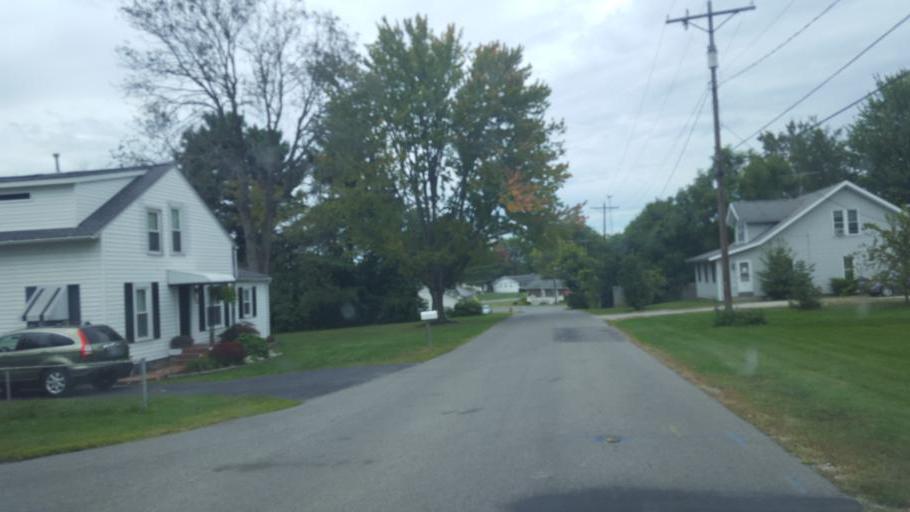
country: US
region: Ohio
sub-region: Delaware County
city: Sunbury
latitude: 40.2454
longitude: -82.8510
